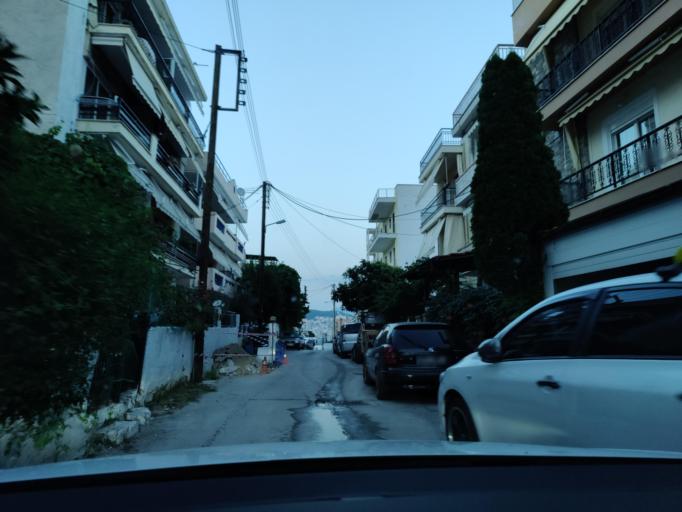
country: GR
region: East Macedonia and Thrace
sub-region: Nomos Kavalas
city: Kavala
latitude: 40.9264
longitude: 24.3859
